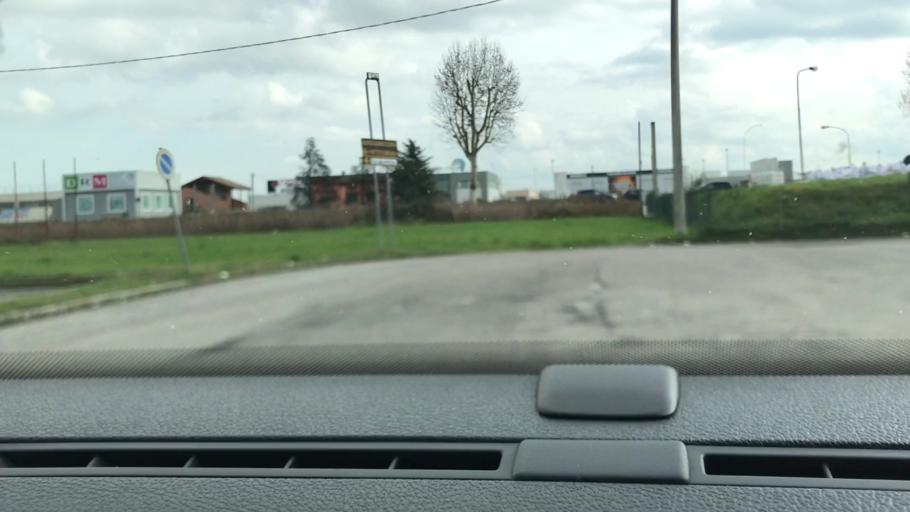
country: IT
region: Veneto
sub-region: Provincia di Rovigo
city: Grignano Polesine
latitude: 45.0369
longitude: 11.7788
